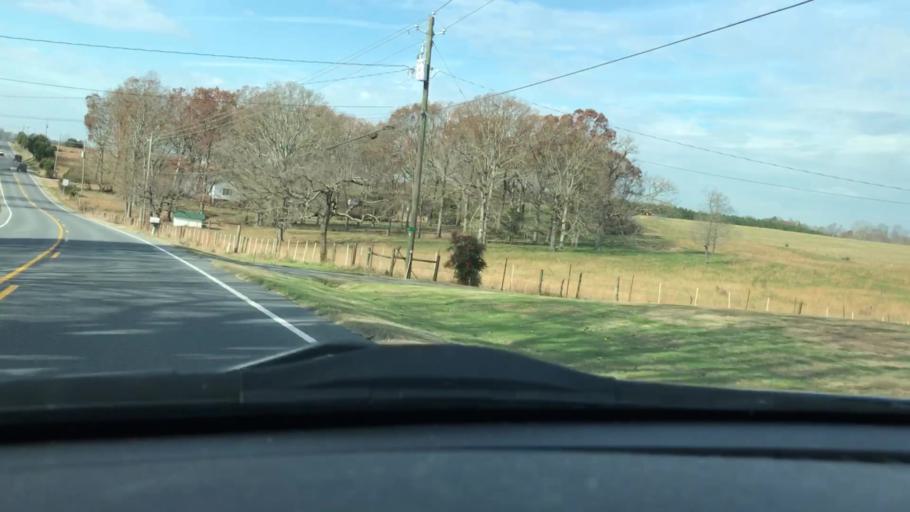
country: US
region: North Carolina
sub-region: Randolph County
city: Asheboro
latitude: 35.6831
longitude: -79.8536
